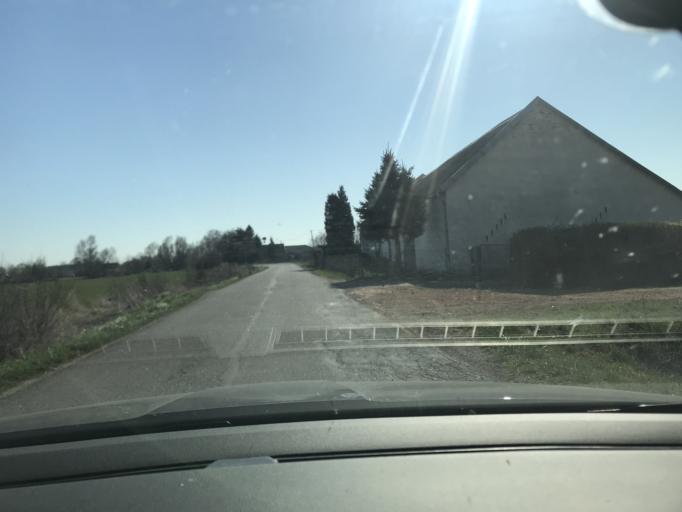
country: PL
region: Pomeranian Voivodeship
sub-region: Powiat nowodworski
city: Sztutowo
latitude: 54.3064
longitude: 19.1516
